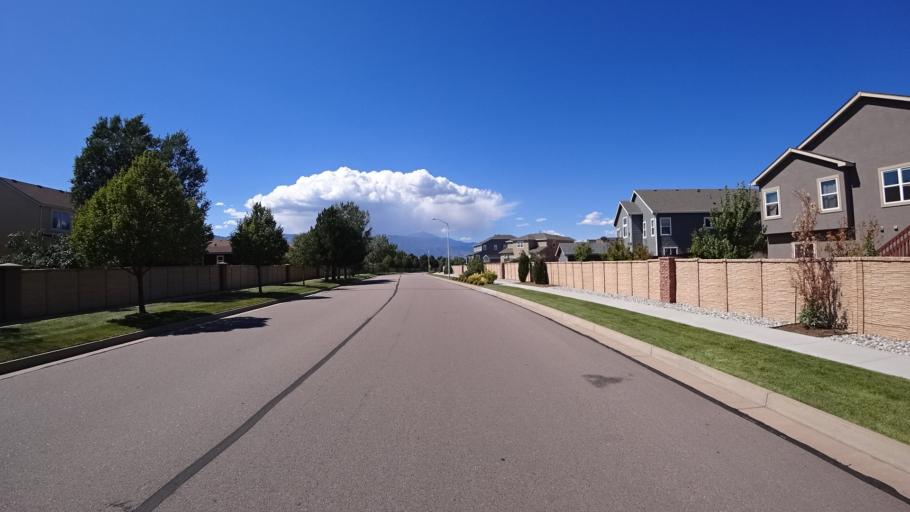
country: US
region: Colorado
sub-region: El Paso County
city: Security-Widefield
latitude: 38.7857
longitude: -104.7308
